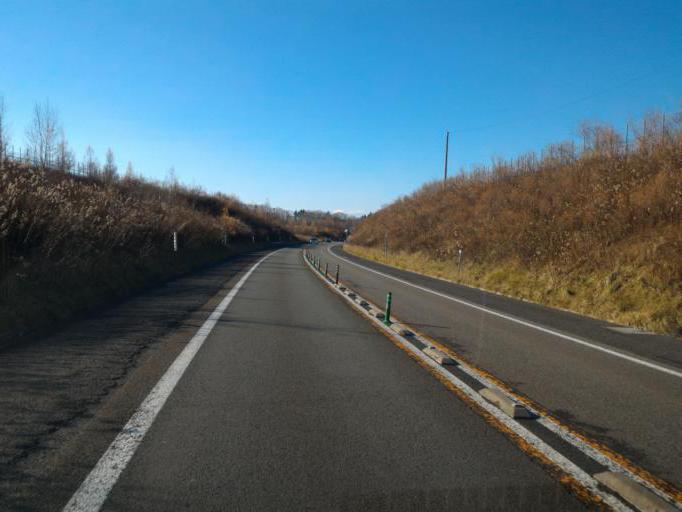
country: JP
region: Hokkaido
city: Chitose
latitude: 42.8957
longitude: 141.8673
